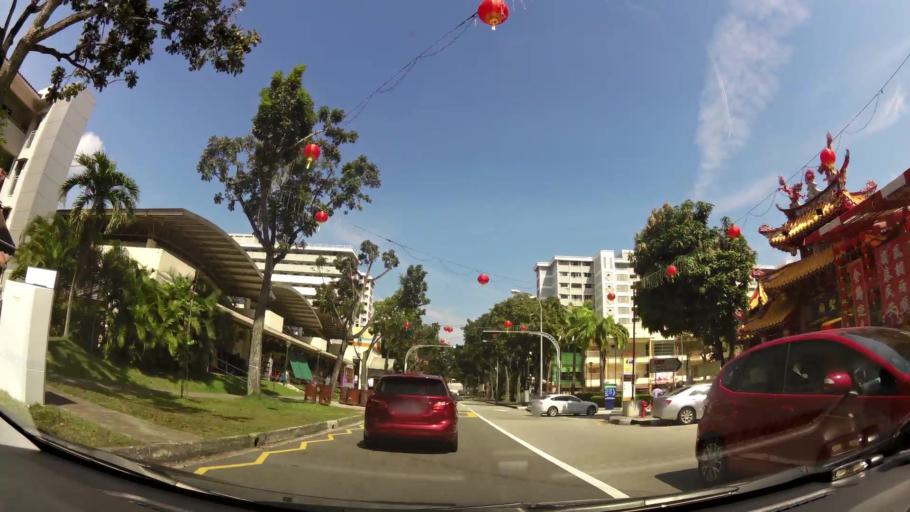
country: SG
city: Singapore
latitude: 1.3807
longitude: 103.8412
